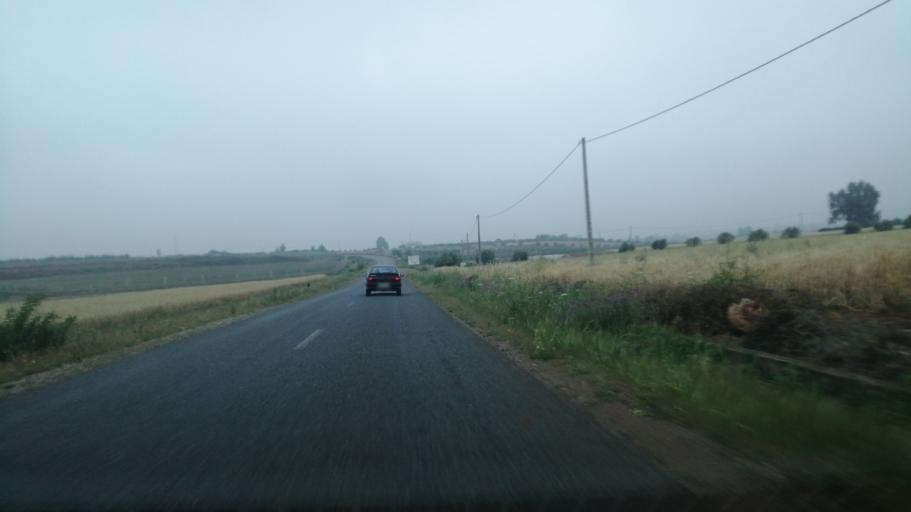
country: MA
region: Rabat-Sale-Zemmour-Zaer
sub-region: Khemisset
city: Tiflet
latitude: 33.7414
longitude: -6.2696
